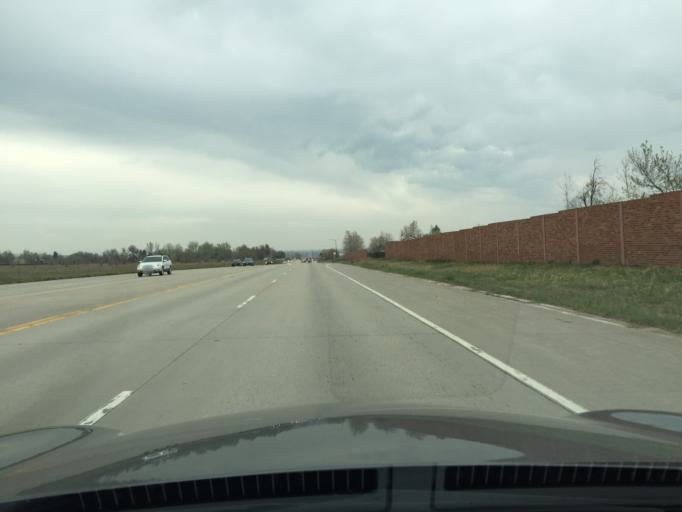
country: US
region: Colorado
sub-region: Boulder County
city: Lafayette
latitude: 40.0079
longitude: -105.1028
